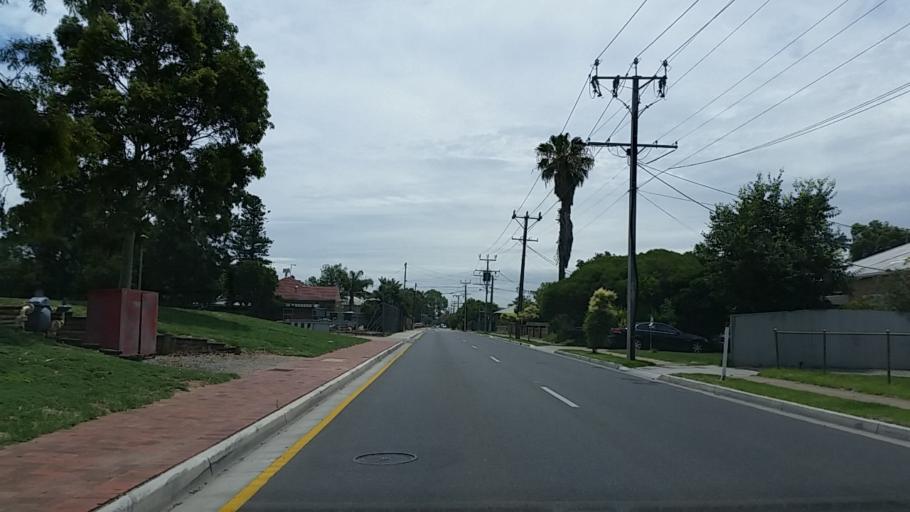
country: AU
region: South Australia
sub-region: Charles Sturt
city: Allenby Gardens
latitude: -34.9002
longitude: 138.5474
